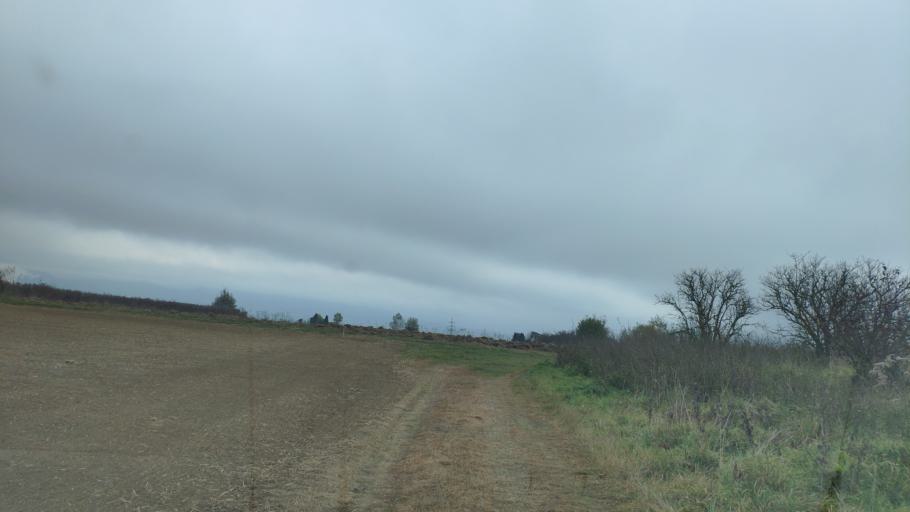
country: SK
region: Presovsky
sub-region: Okres Presov
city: Presov
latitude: 49.0137
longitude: 21.2103
